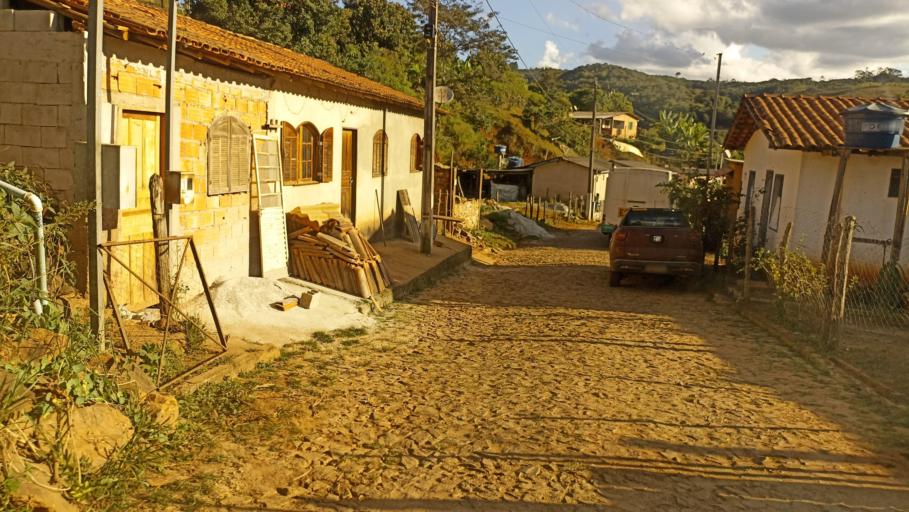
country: BR
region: Minas Gerais
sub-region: Ouro Preto
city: Ouro Preto
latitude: -20.3090
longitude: -43.5781
